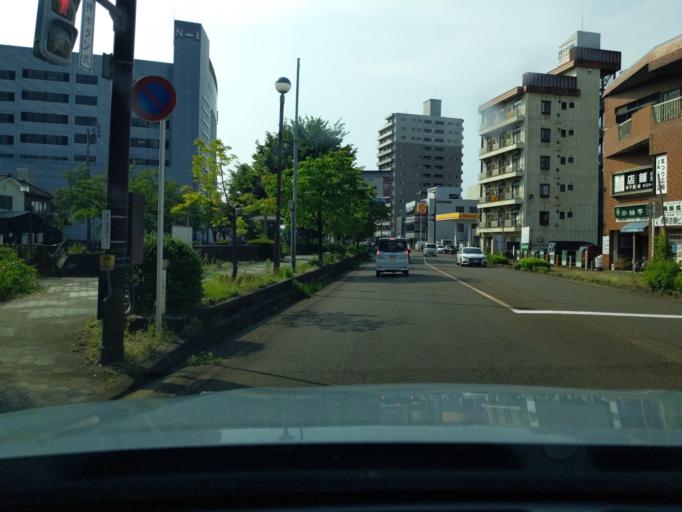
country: JP
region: Niigata
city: Nagaoka
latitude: 37.4436
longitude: 138.8499
